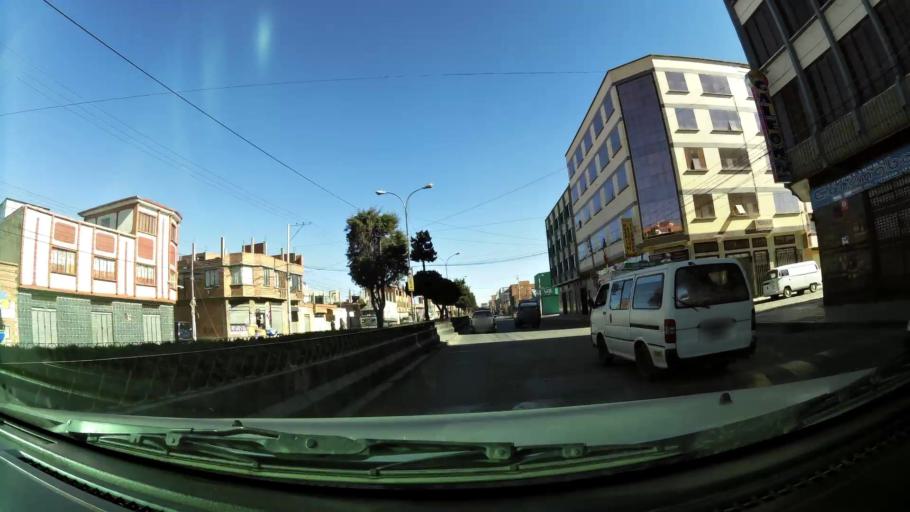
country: BO
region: La Paz
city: La Paz
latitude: -16.5288
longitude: -68.1967
